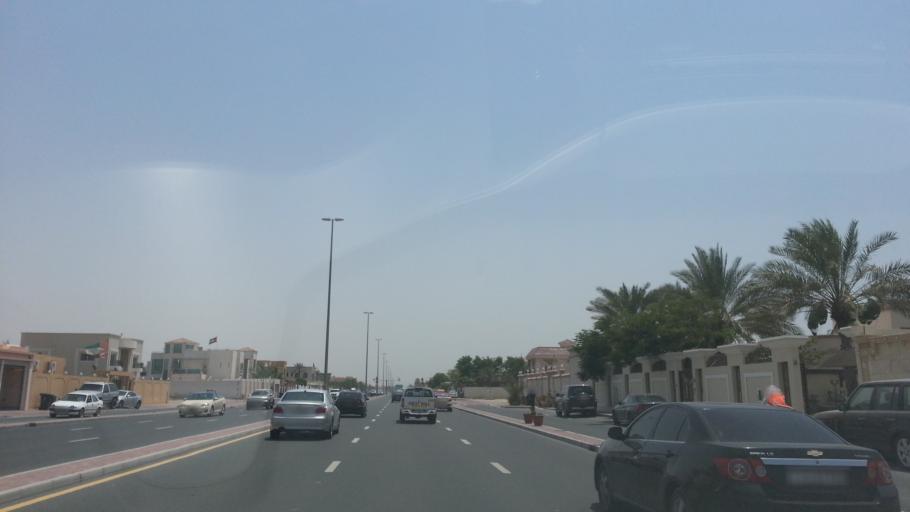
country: AE
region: Dubai
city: Dubai
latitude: 25.1085
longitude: 55.2186
